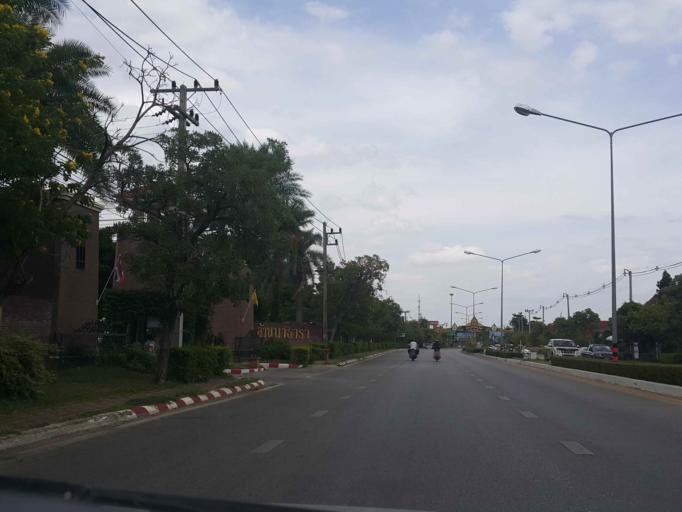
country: TH
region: Chiang Mai
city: Hang Dong
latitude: 18.7288
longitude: 98.9445
